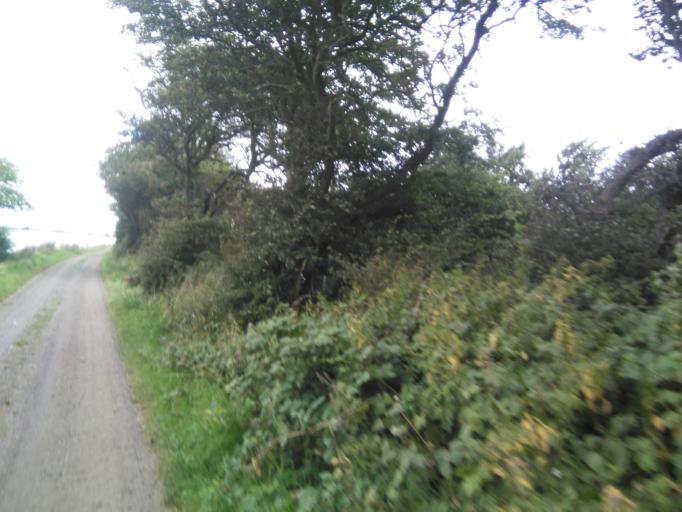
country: DK
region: Central Jutland
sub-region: Odder Kommune
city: Odder
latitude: 55.8627
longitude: 10.1398
